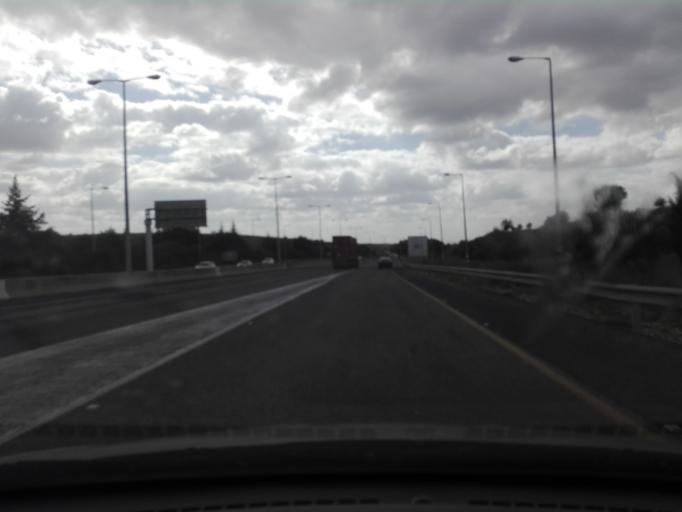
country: IL
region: Haifa
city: Daliyat el Karmil
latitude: 32.6309
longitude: 35.0630
